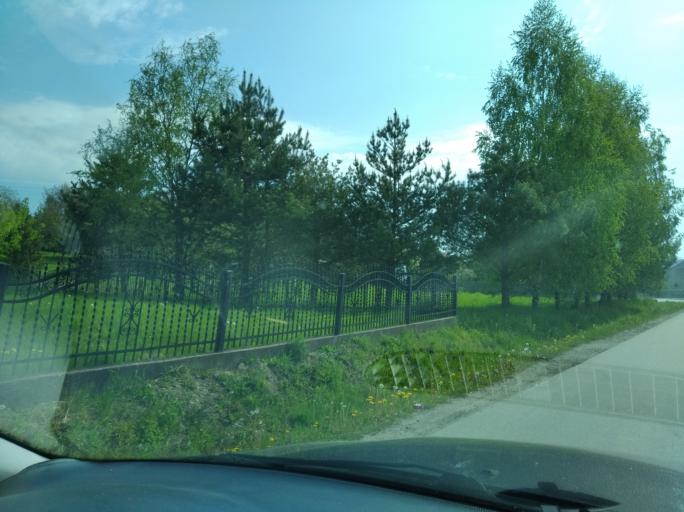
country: PL
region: Subcarpathian Voivodeship
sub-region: Powiat jaroslawski
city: Pruchnik
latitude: 49.9053
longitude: 22.5212
